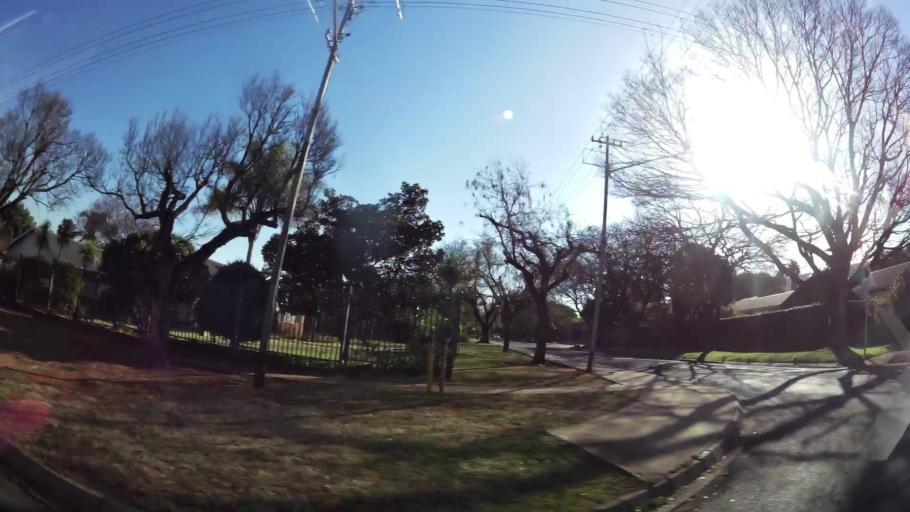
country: ZA
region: Gauteng
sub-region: City of Tshwane Metropolitan Municipality
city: Pretoria
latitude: -25.6983
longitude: 28.2563
